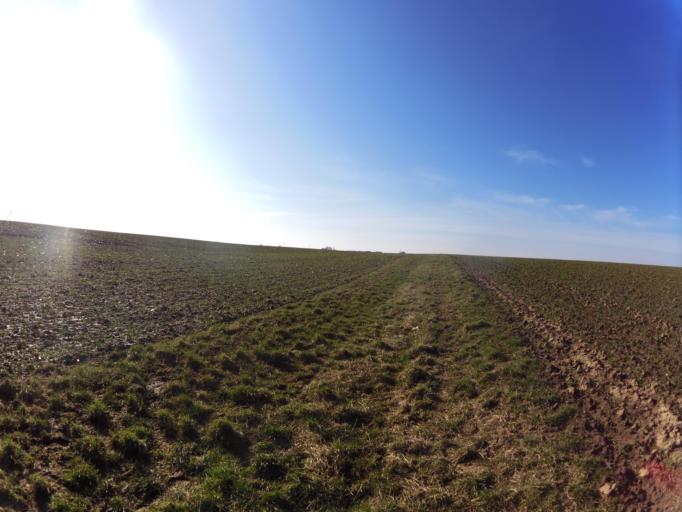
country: DE
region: Bavaria
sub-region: Regierungsbezirk Unterfranken
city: Giebelstadt
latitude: 49.6781
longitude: 9.9725
